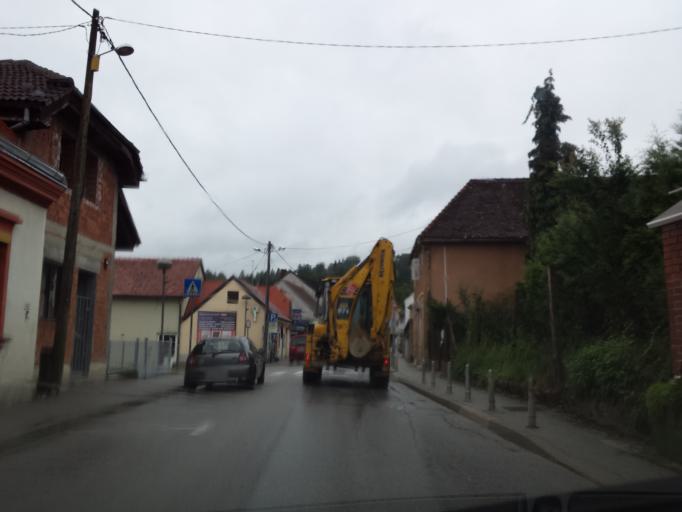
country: HR
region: Zagrebacka
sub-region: Grad Samobor
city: Samobor
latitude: 45.8042
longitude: 15.7097
